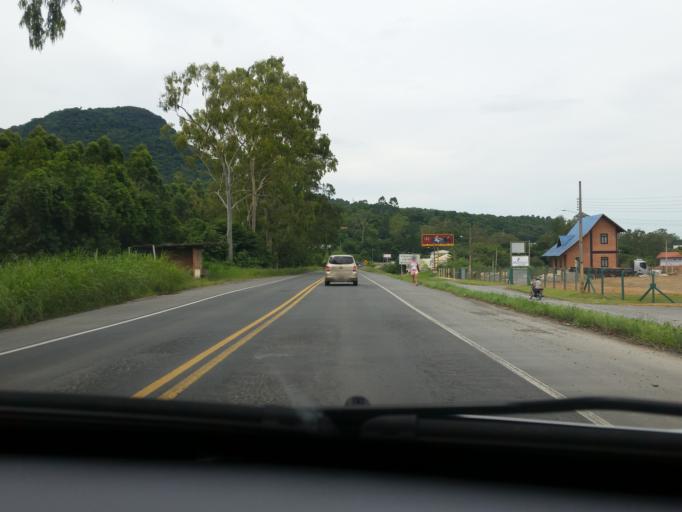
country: BR
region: Santa Catarina
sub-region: Rio Do Sul
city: Rio do Sul
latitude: -27.1919
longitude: -49.6217
